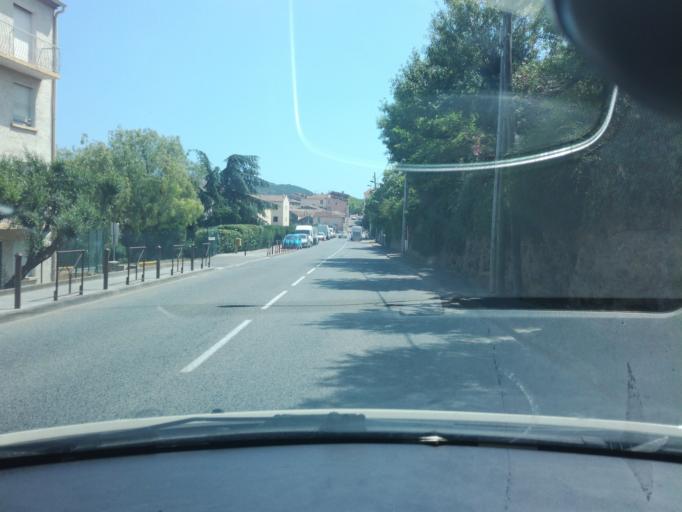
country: FR
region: Provence-Alpes-Cote d'Azur
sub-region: Departement du Var
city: Le Muy
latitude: 43.4764
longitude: 6.5667
